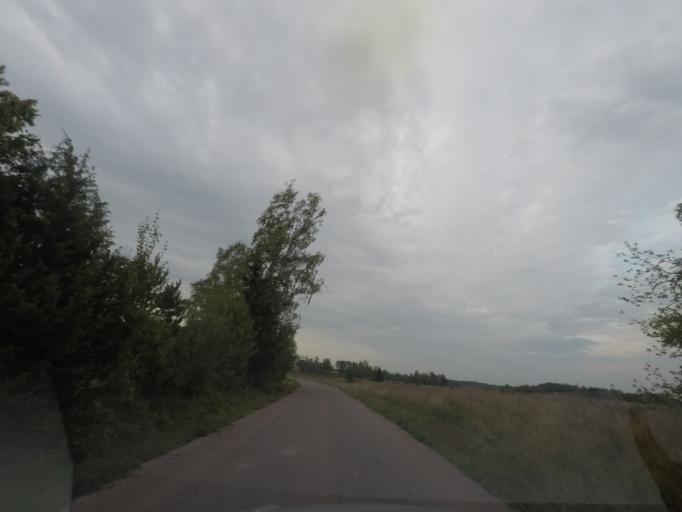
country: SE
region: Vaestmanland
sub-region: Hallstahammars Kommun
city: Kolback
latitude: 59.4989
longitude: 16.1893
